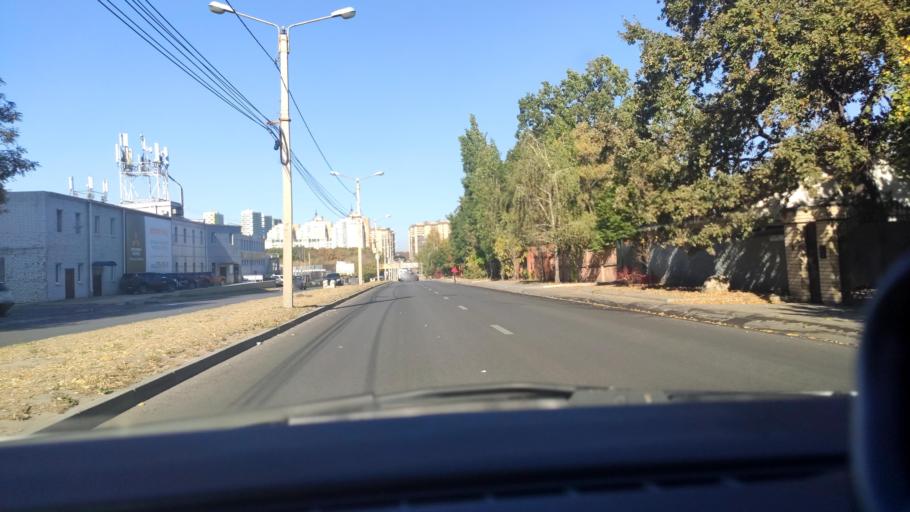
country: RU
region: Voronezj
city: Voronezh
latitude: 51.7050
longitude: 39.1960
